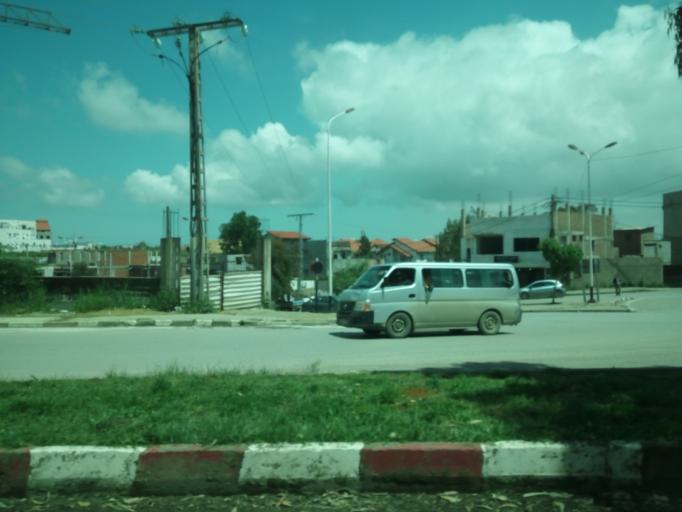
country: DZ
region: Tipaza
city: Saoula
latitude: 36.7300
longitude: 2.9971
